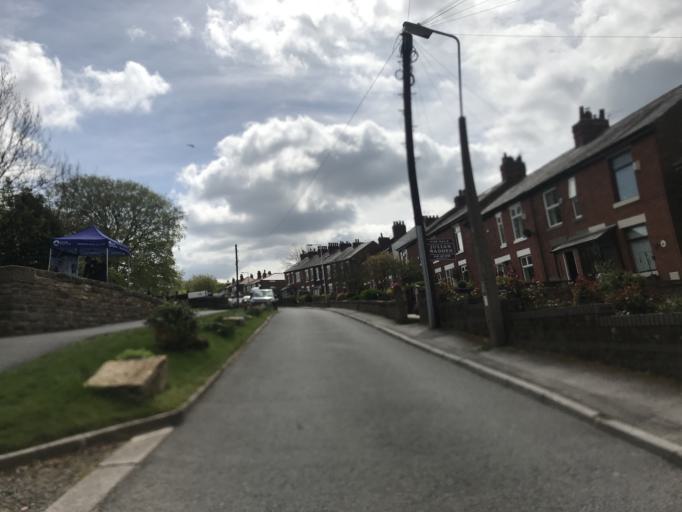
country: GB
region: England
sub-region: Borough of Stockport
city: Marple
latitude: 53.3937
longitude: -2.0601
